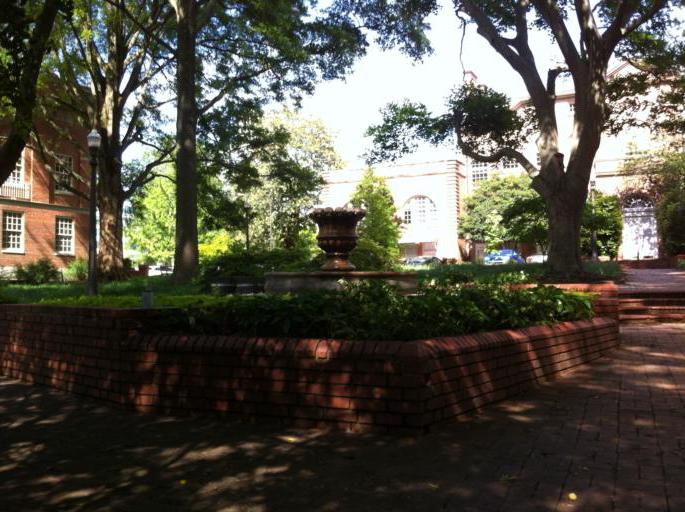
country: US
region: North Carolina
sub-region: Wake County
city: West Raleigh
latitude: 35.7855
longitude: -78.6647
